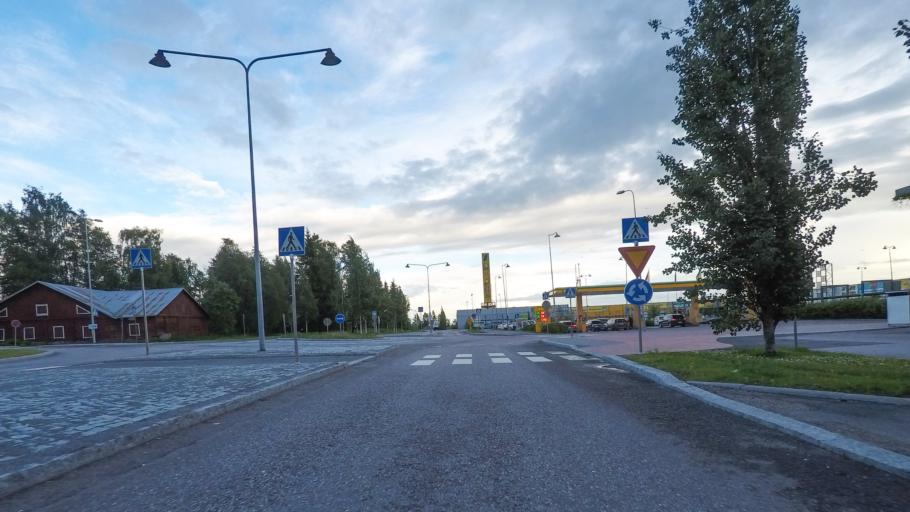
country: FI
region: Paijanne Tavastia
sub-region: Lahti
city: Lahti
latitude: 60.9355
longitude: 25.6348
